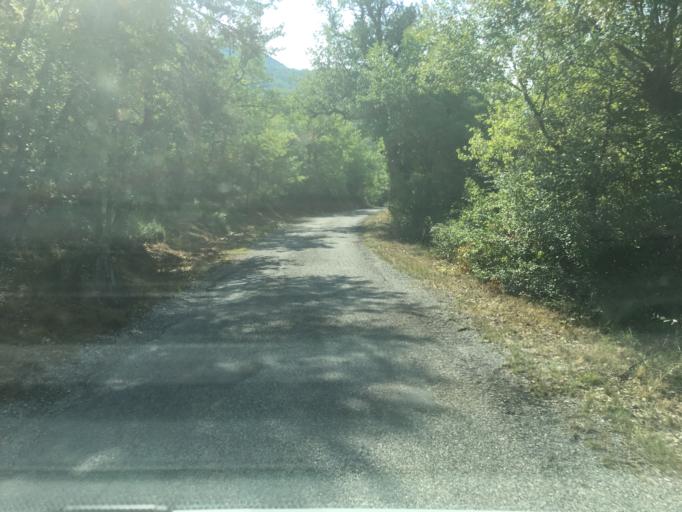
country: FR
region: Provence-Alpes-Cote d'Azur
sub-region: Departement des Alpes-de-Haute-Provence
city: Mallemoisson
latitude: 43.9281
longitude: 6.1901
